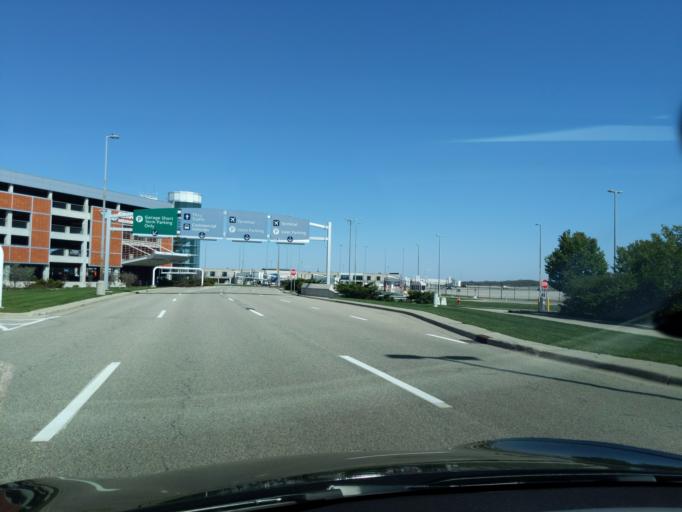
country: US
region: Michigan
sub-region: Kent County
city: Forest Hills
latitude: 42.8838
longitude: -85.5330
